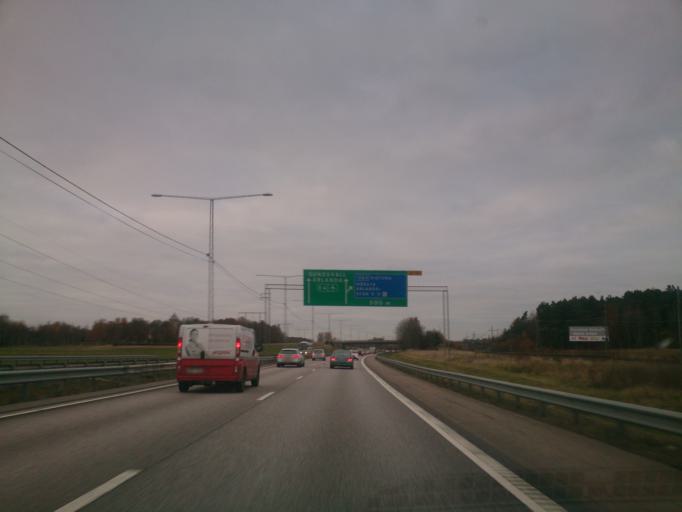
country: SE
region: Stockholm
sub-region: Sigtuna Kommun
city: Rosersberg
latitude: 59.5896
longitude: 17.8978
